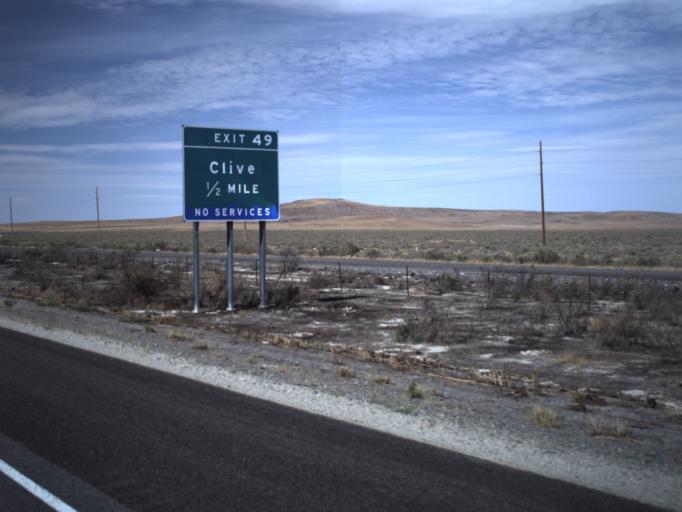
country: US
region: Utah
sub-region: Tooele County
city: Grantsville
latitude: 40.7371
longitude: -113.0968
